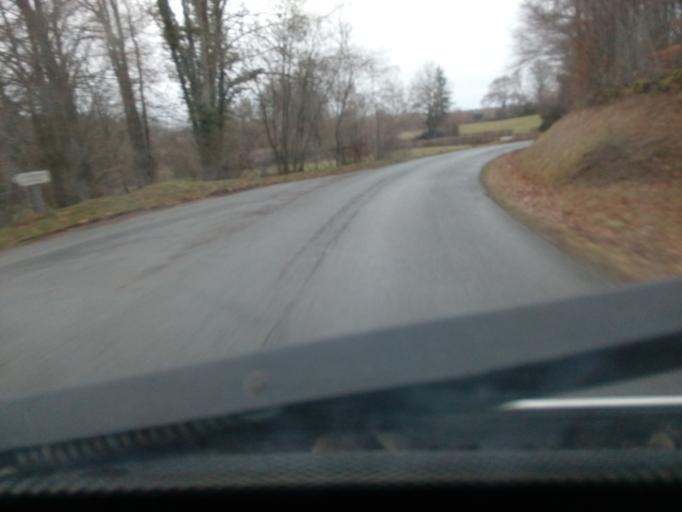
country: FR
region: Limousin
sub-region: Departement de la Creuse
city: Felletin
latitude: 45.8419
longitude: 2.2395
